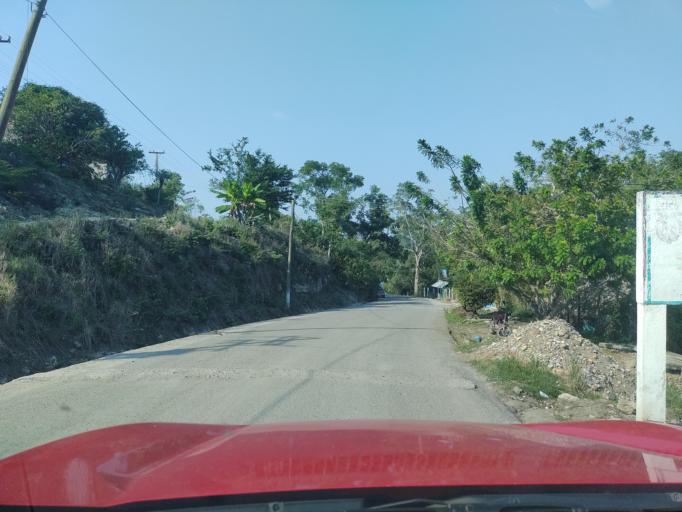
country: MX
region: Veracruz
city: Agua Dulce
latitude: 20.3686
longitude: -97.1842
